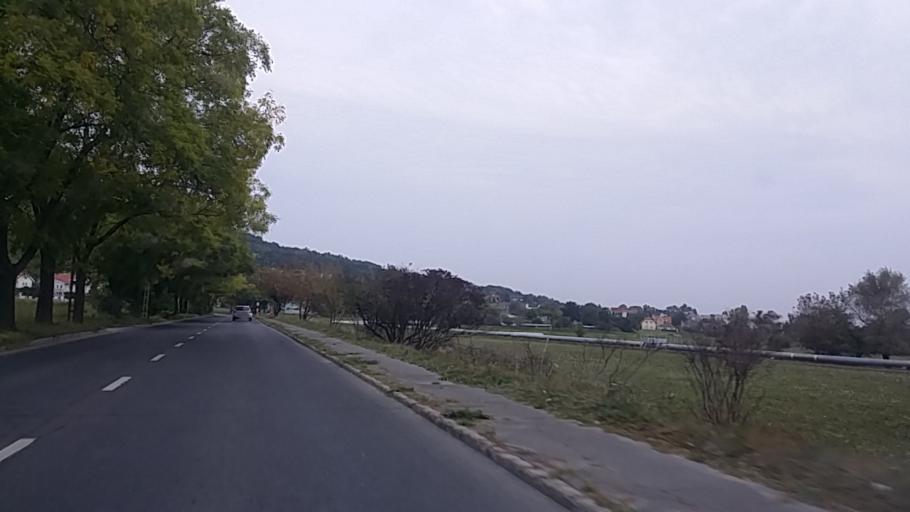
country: HU
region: Pest
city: Urom
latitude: 47.5759
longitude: 19.0314
